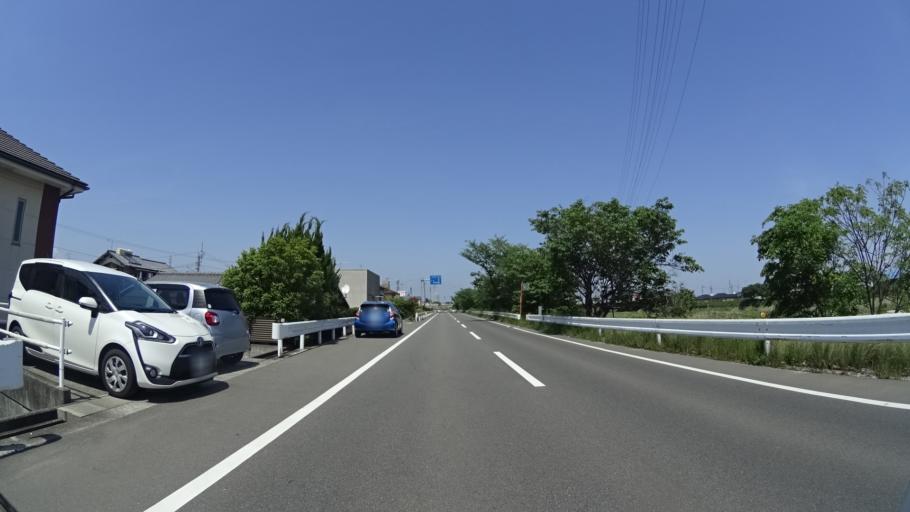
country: JP
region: Ehime
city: Hojo
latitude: 34.0448
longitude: 132.9832
